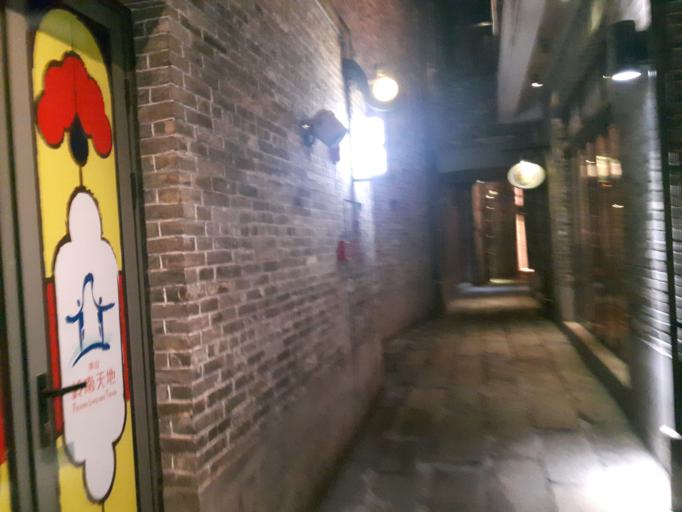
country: CN
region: Guangdong
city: Zumiao
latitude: 23.0321
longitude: 113.1105
